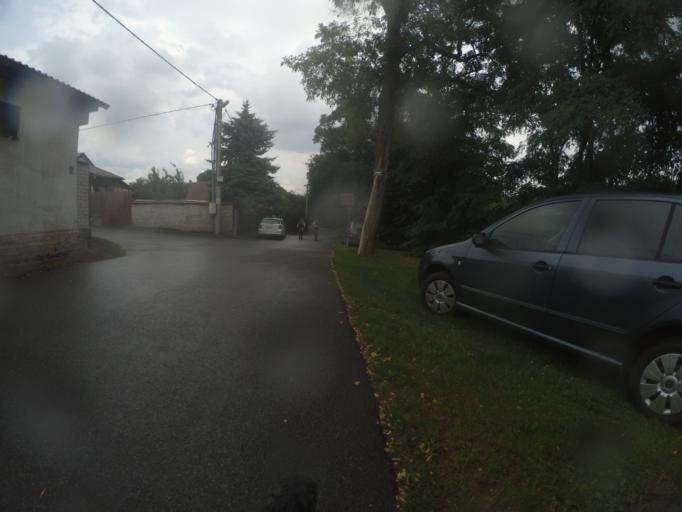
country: CZ
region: Central Bohemia
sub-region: Okres Melnik
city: Melnik
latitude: 50.3233
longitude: 14.4580
